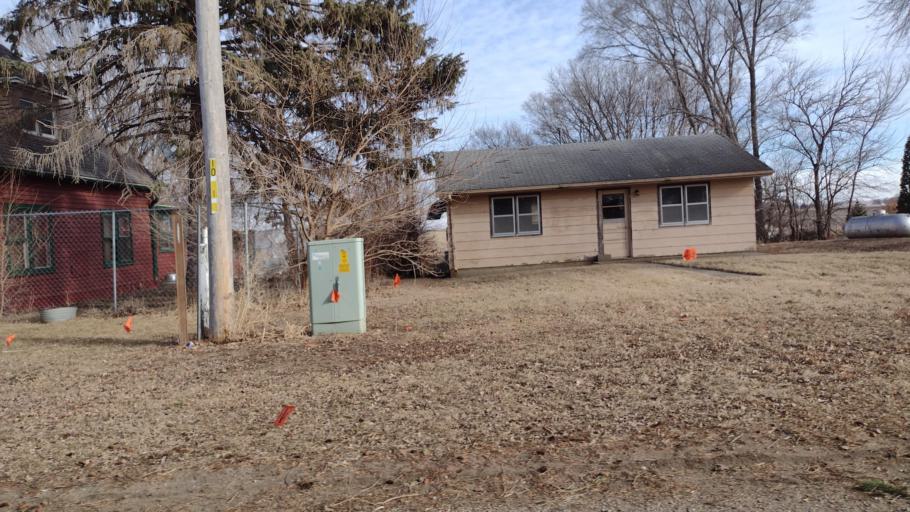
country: US
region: South Dakota
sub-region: Union County
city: Beresford
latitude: 42.9614
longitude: -96.8055
